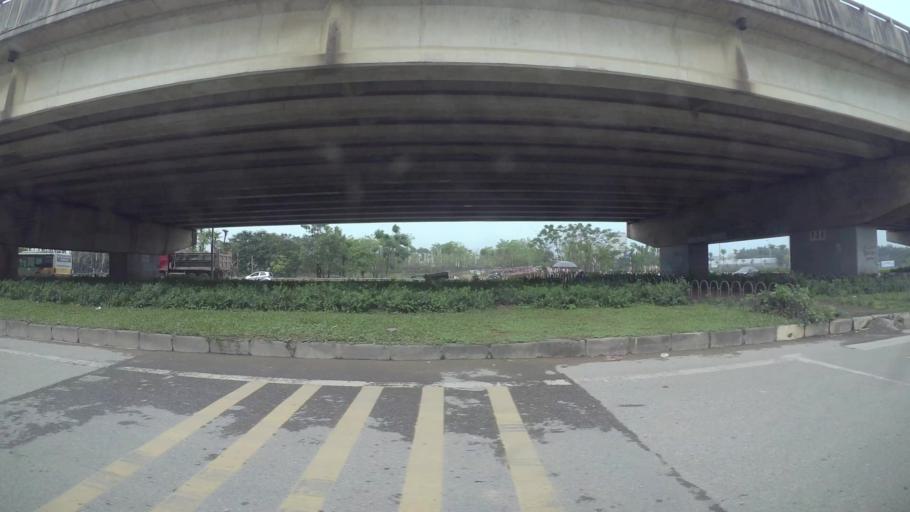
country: VN
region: Ha Noi
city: Tay Ho
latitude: 21.1249
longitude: 105.7816
